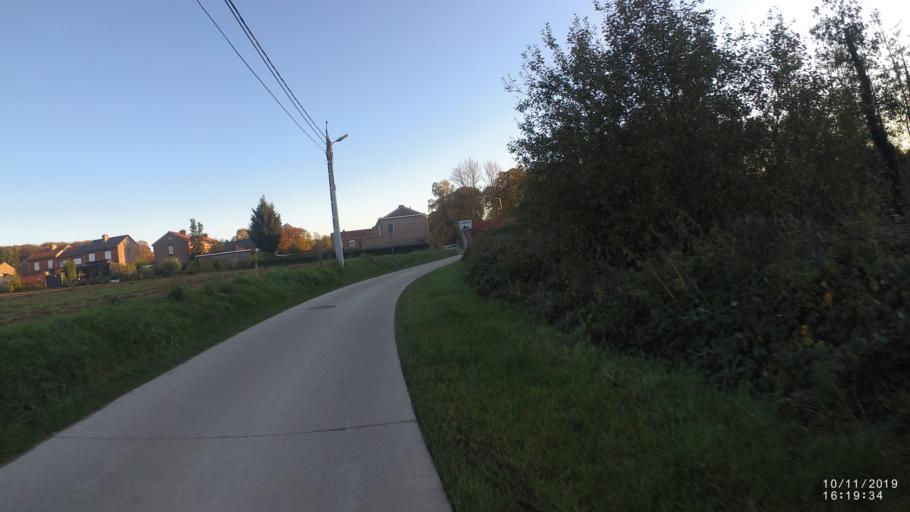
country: BE
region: Flanders
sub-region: Provincie Vlaams-Brabant
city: Lubbeek
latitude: 50.8850
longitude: 4.8506
